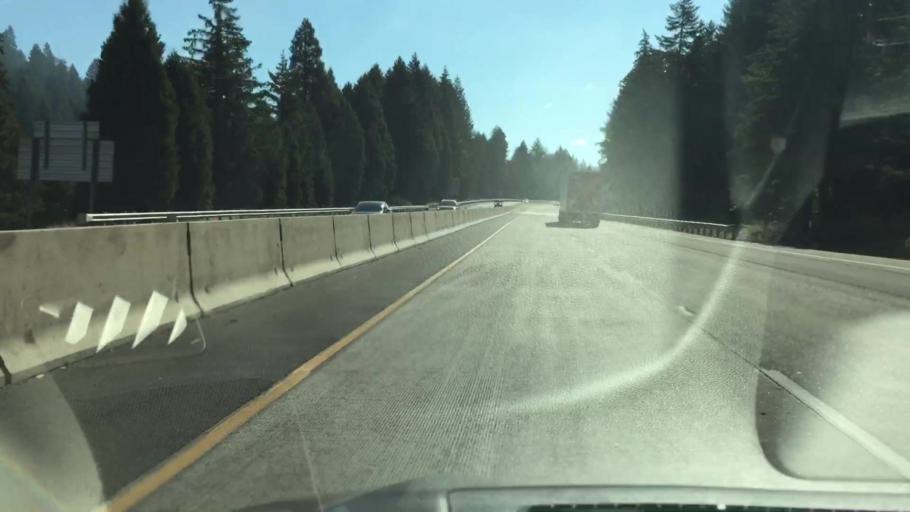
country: US
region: Oregon
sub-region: Douglas County
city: Drain
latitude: 43.7077
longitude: -123.2149
